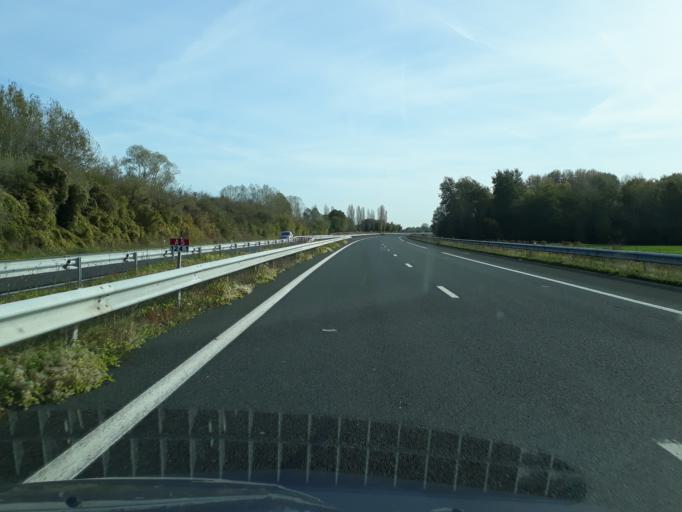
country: FR
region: Champagne-Ardenne
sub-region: Departement de l'Aube
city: Saint-Pouange
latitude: 48.2334
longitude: 4.0460
